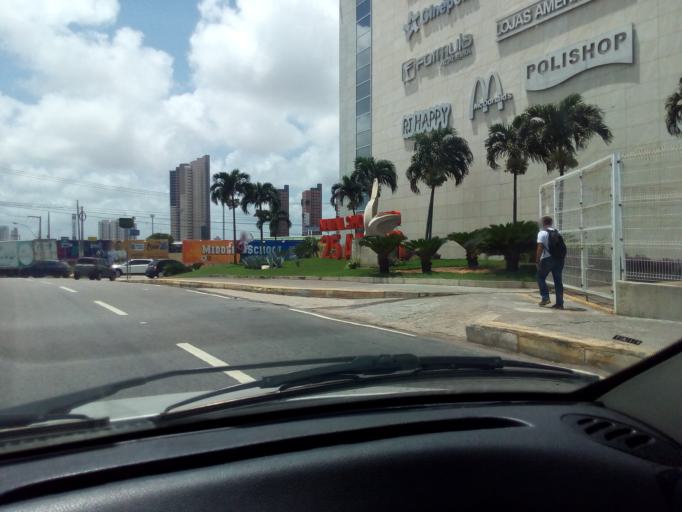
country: BR
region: Rio Grande do Norte
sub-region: Natal
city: Natal
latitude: -5.8420
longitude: -35.2102
